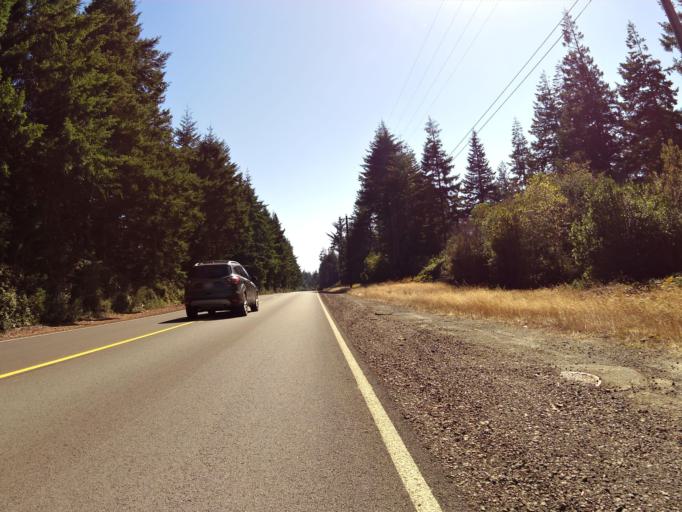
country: US
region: Oregon
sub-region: Coos County
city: Bandon
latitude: 43.2006
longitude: -124.3661
